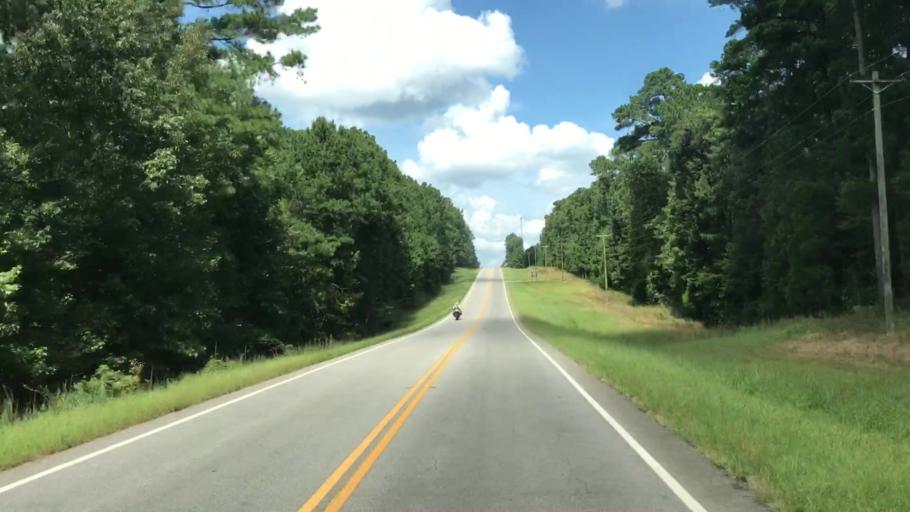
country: US
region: Georgia
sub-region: Greene County
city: Greensboro
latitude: 33.6570
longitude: -83.2392
